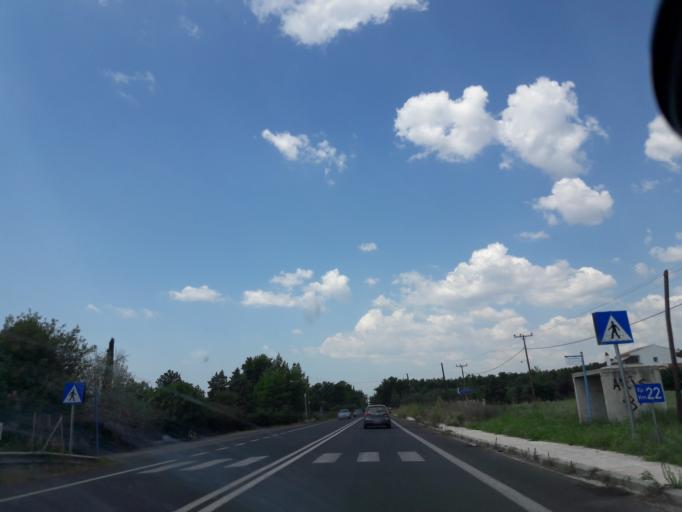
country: GR
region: Central Macedonia
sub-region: Nomos Thessalonikis
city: Souroti
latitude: 40.5107
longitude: 23.0810
